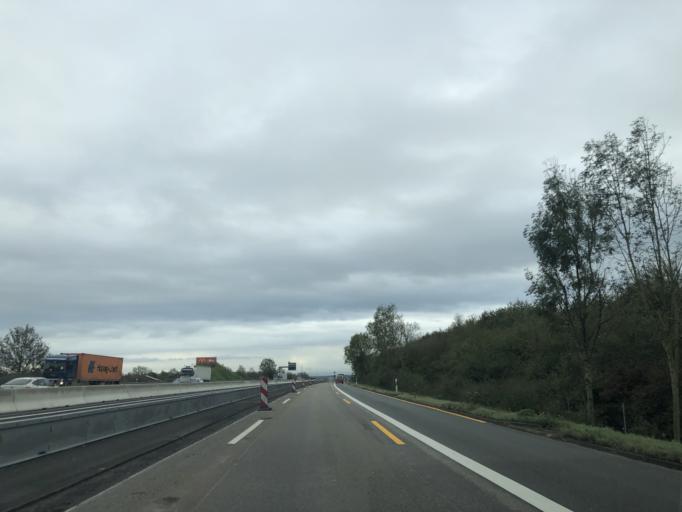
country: DE
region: Hesse
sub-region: Regierungsbezirk Darmstadt
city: Rodgau
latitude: 50.0507
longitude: 8.9213
